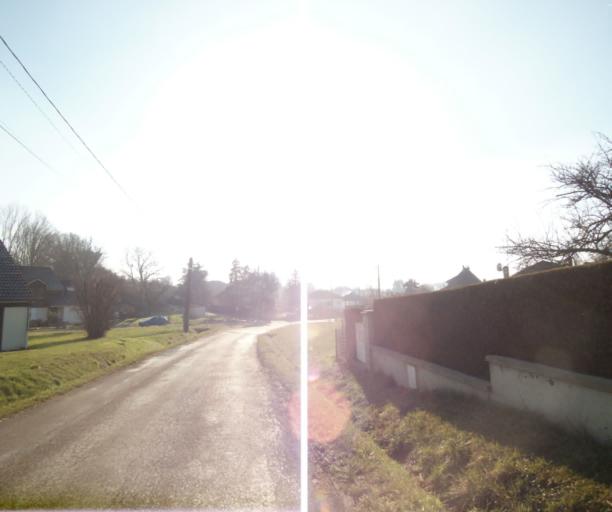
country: FR
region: Champagne-Ardenne
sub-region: Departement de la Haute-Marne
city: Wassy
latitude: 48.5016
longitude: 4.9573
